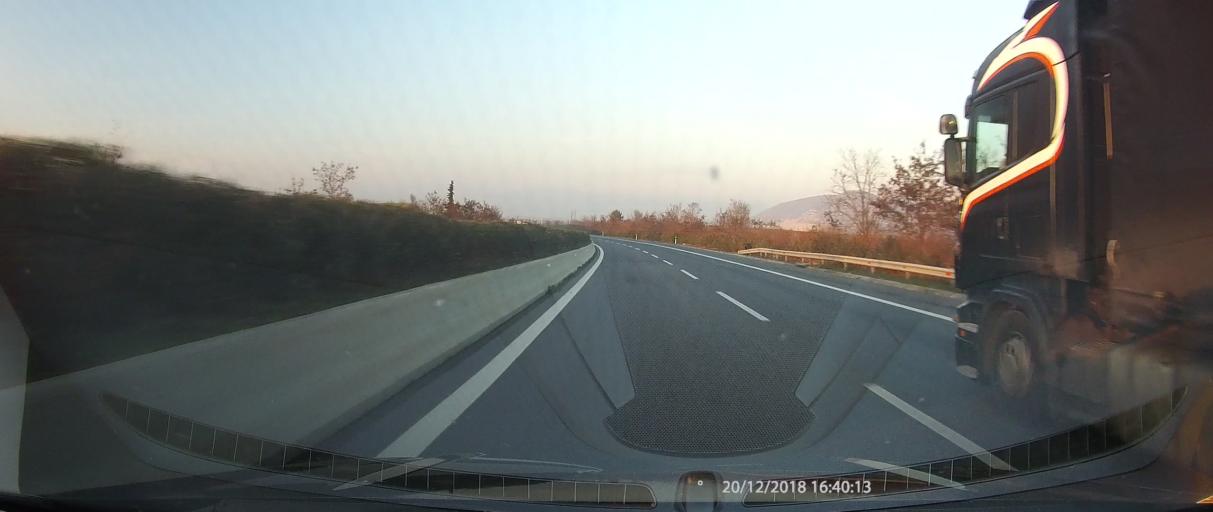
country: GR
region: Thessaly
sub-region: Nomos Magnisias
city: Velestino
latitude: 39.3712
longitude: 22.7706
